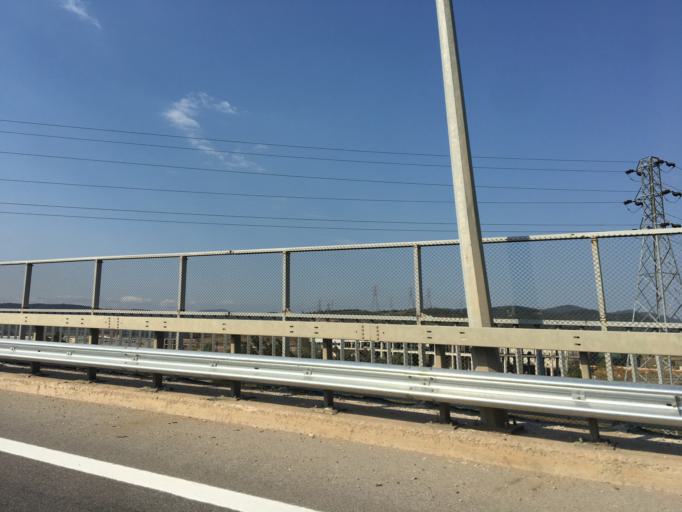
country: TR
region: Bursa
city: Yenice
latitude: 40.2021
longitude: 29.3521
